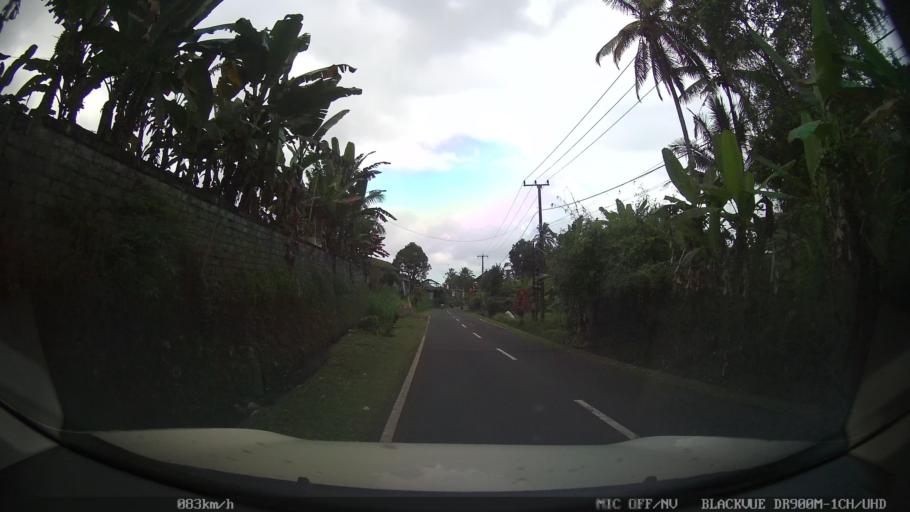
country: ID
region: Bali
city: Penebel
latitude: -8.4104
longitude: 115.1455
